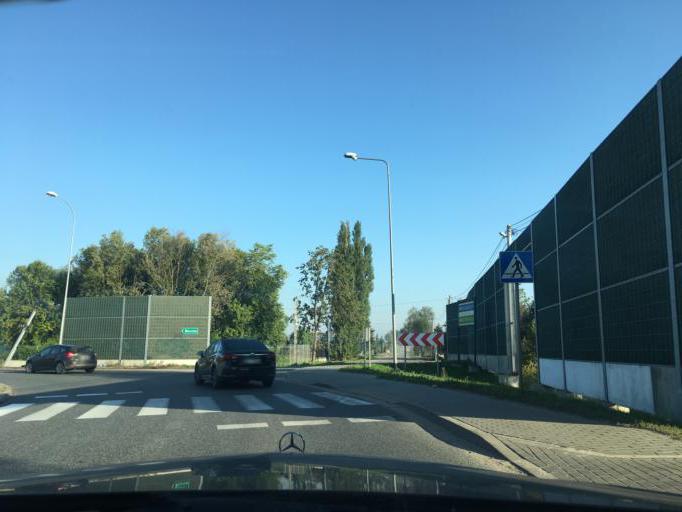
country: PL
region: Masovian Voivodeship
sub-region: Powiat grodziski
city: Grodzisk Mazowiecki
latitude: 52.1413
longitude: 20.6165
